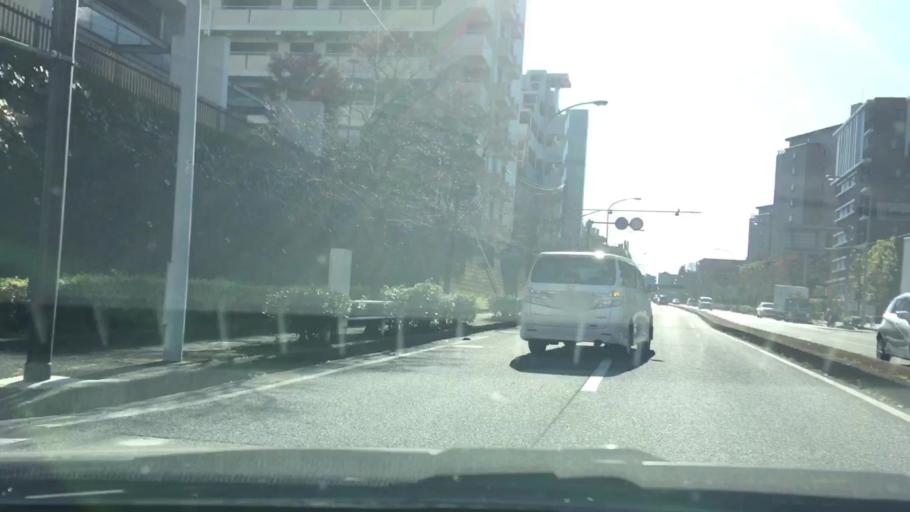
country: JP
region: Kanagawa
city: Yokohama
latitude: 35.5409
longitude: 139.5865
